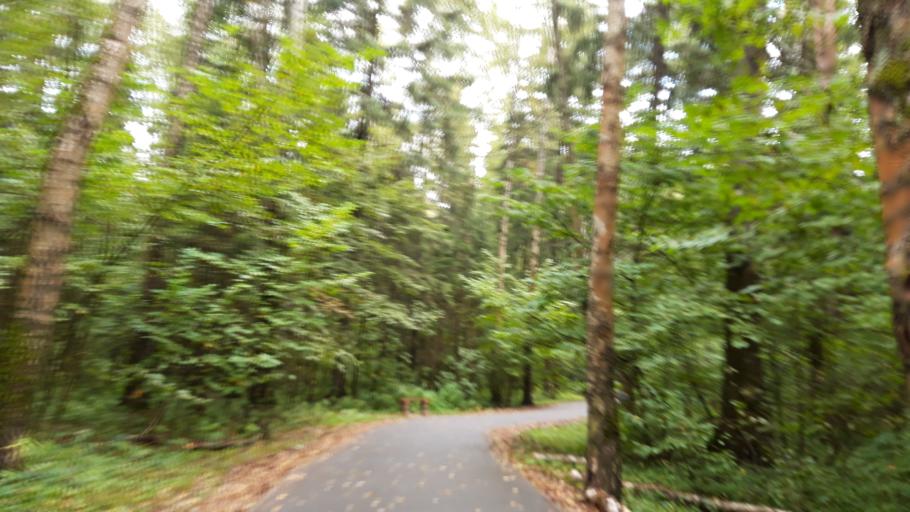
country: RU
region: Moscow
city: Zelenograd
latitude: 55.9838
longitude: 37.1950
